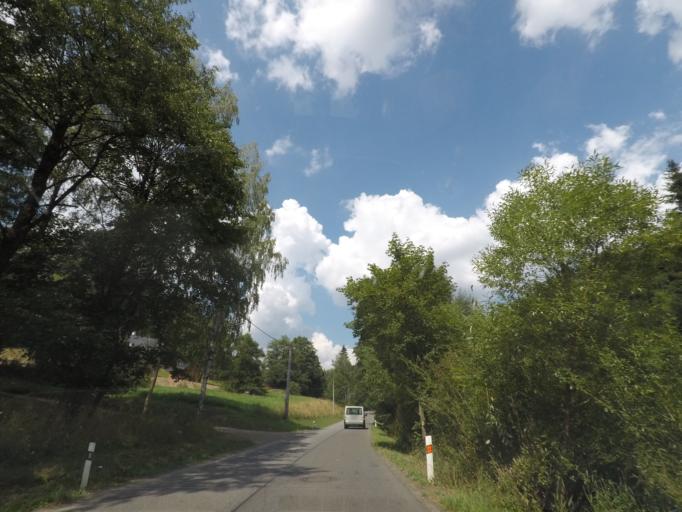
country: CZ
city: Radvanice
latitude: 50.6204
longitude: 16.1037
